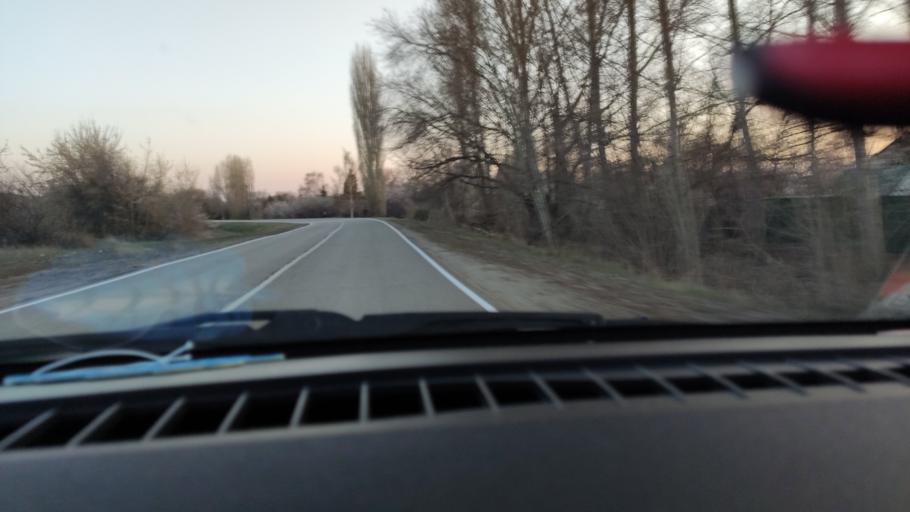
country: RU
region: Saratov
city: Privolzhskiy
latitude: 51.2200
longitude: 45.9193
